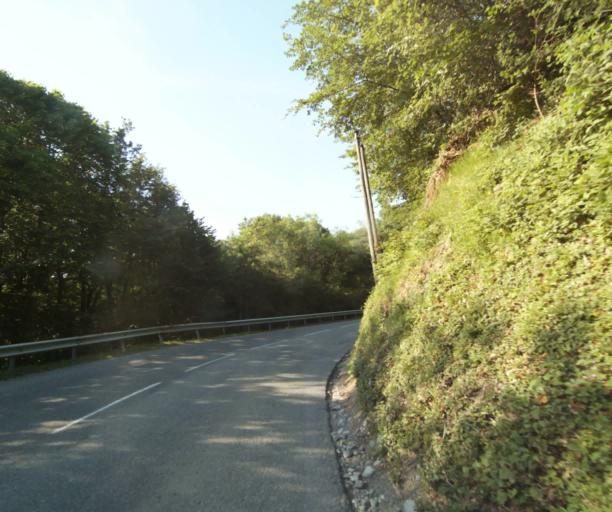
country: FR
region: Rhone-Alpes
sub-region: Departement de la Haute-Savoie
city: Armoy
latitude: 46.3594
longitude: 6.5156
